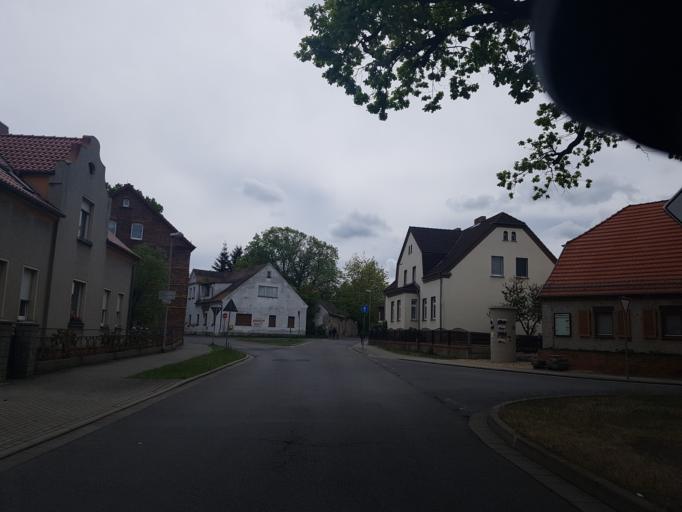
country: DE
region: Brandenburg
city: Tschernitz
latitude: 51.6179
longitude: 14.6012
